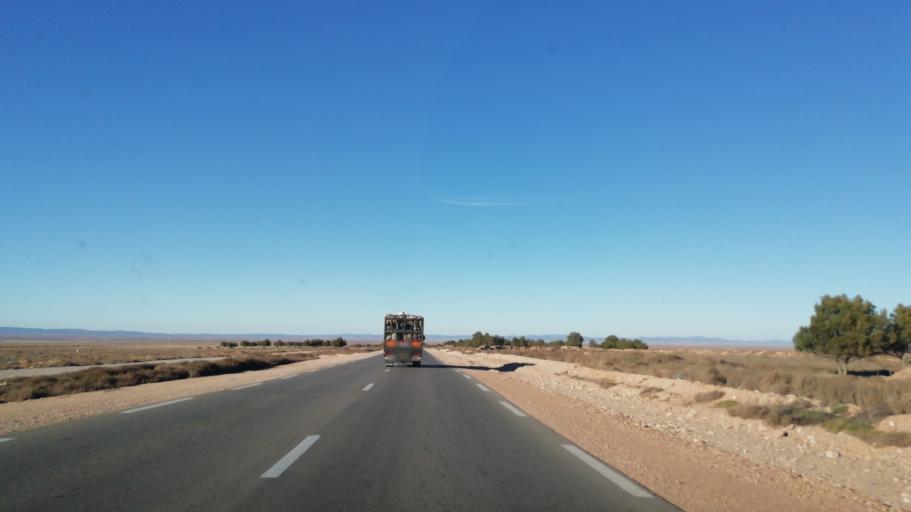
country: DZ
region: Tlemcen
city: Sebdou
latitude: 34.3151
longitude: -1.2626
